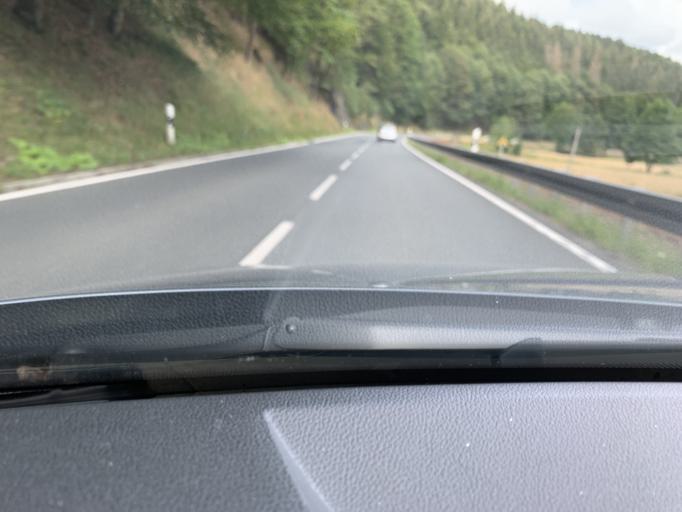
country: DE
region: Thuringia
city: Judenbach
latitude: 50.4076
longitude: 11.1851
